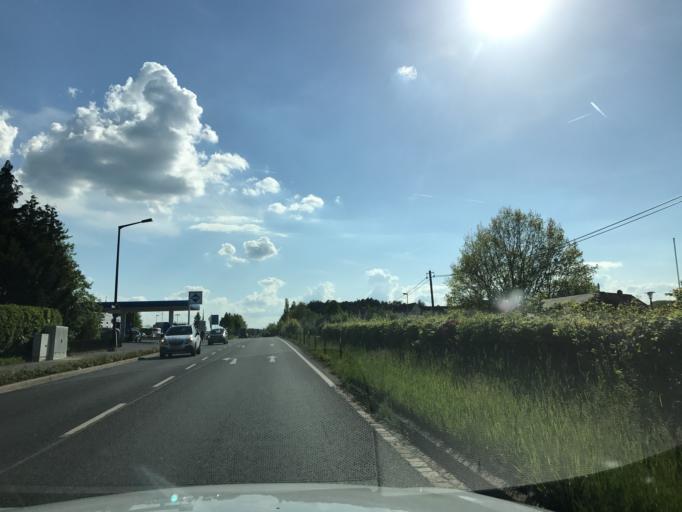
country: DE
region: Bavaria
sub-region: Upper Franconia
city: Igensdorf
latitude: 49.5899
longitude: 11.2179
